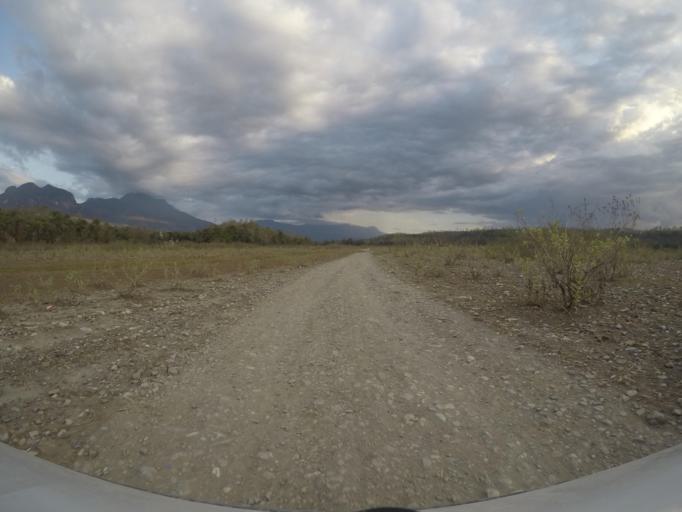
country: TL
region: Bobonaro
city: Maliana
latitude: -8.8937
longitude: 125.2086
